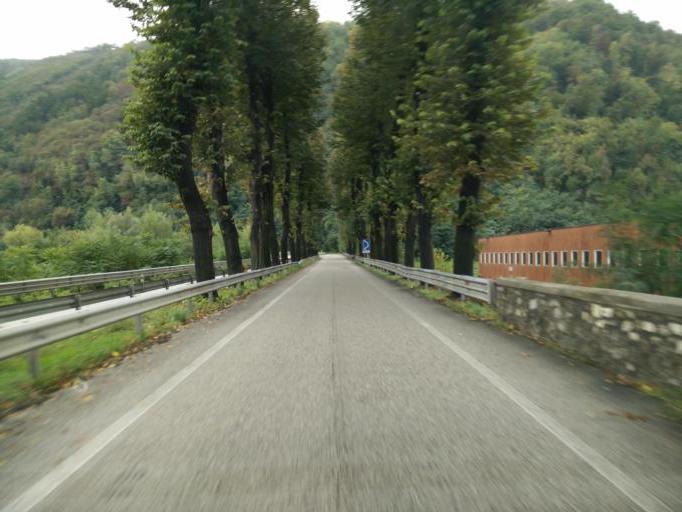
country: IT
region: Tuscany
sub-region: Provincia di Lucca
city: Valdottavo
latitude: 43.9412
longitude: 10.4953
